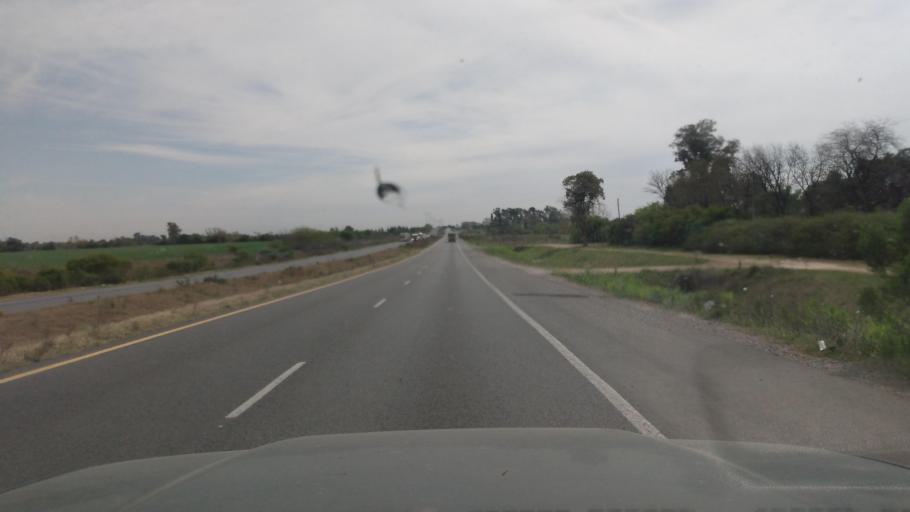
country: AR
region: Buenos Aires
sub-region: Partido de Lujan
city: Lujan
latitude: -34.4777
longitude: -59.0634
